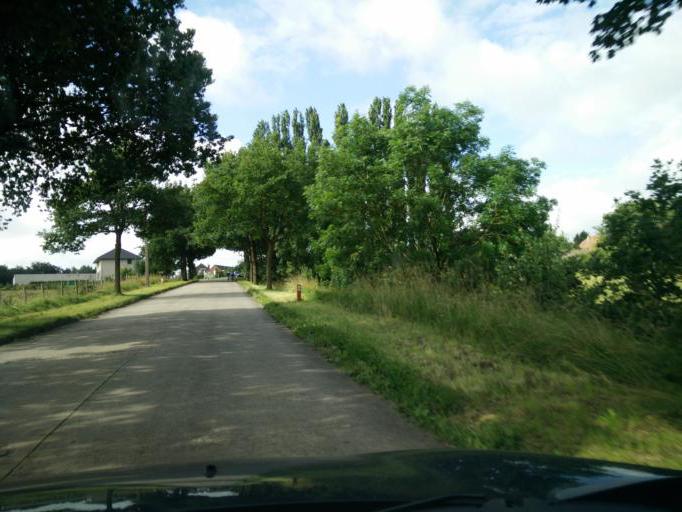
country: BE
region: Wallonia
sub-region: Province du Hainaut
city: Flobecq
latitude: 50.7753
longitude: 3.7338
